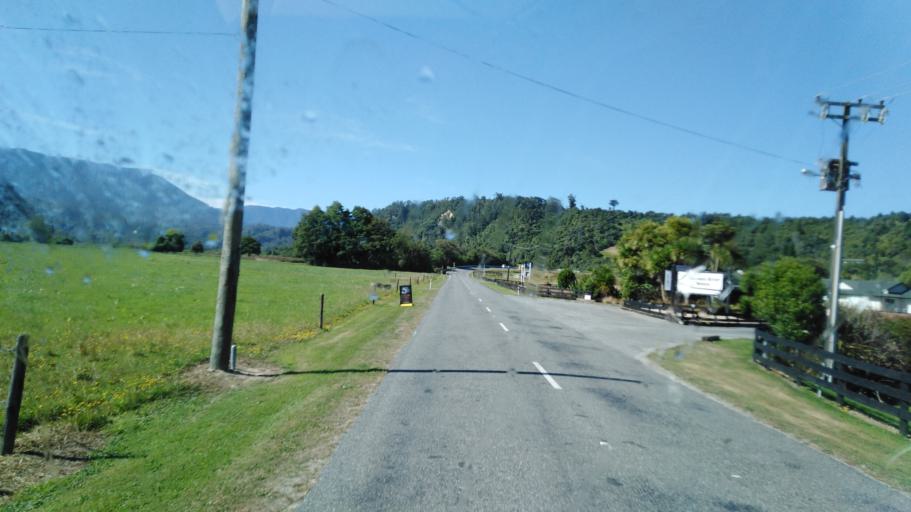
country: NZ
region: West Coast
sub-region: Buller District
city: Westport
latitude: -41.2570
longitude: 172.1312
